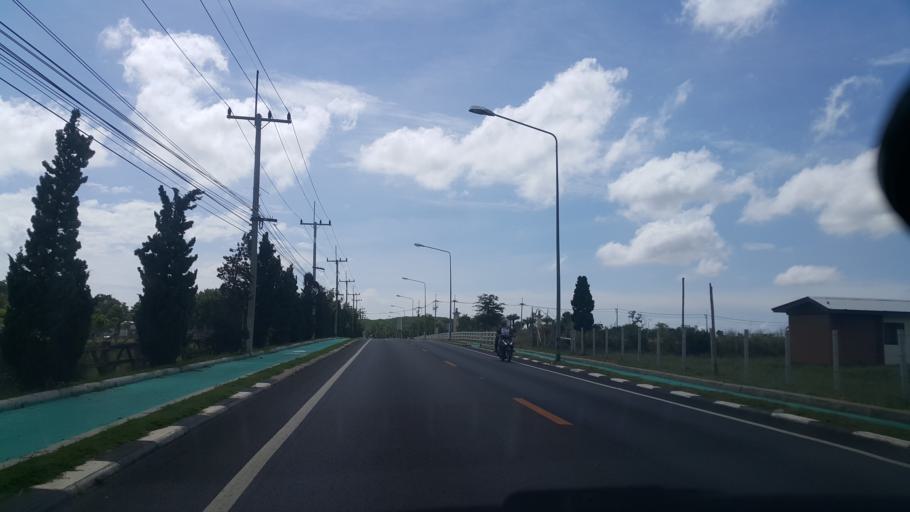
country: TH
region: Rayong
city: Ban Chang
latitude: 12.7642
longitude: 100.9610
